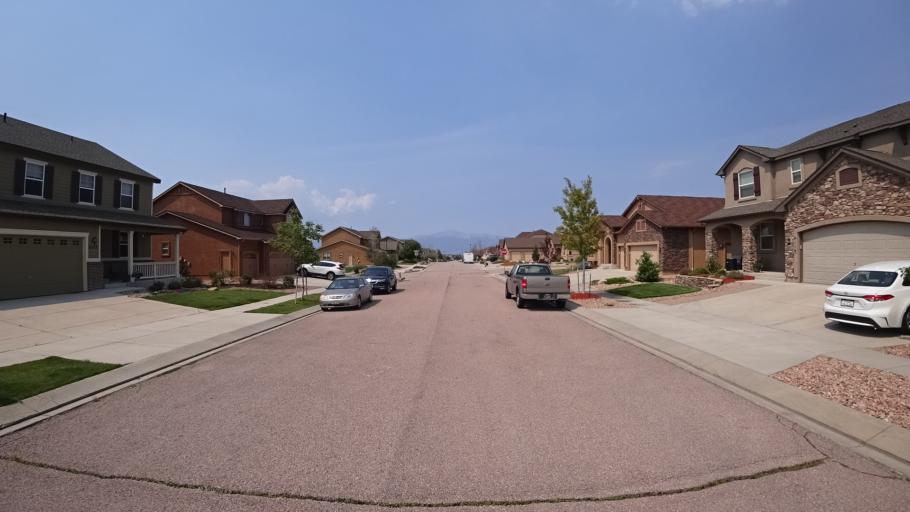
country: US
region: Colorado
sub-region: El Paso County
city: Black Forest
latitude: 38.9666
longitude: -104.7168
